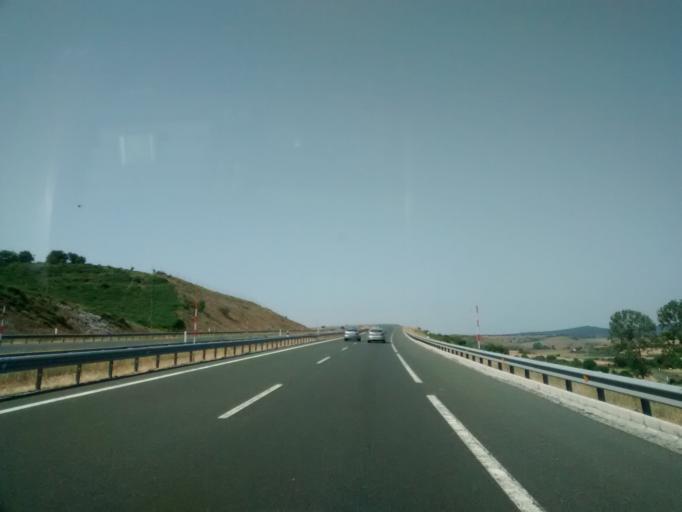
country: ES
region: Cantabria
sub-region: Provincia de Cantabria
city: Mataporquera
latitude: 42.8881
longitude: -4.1321
